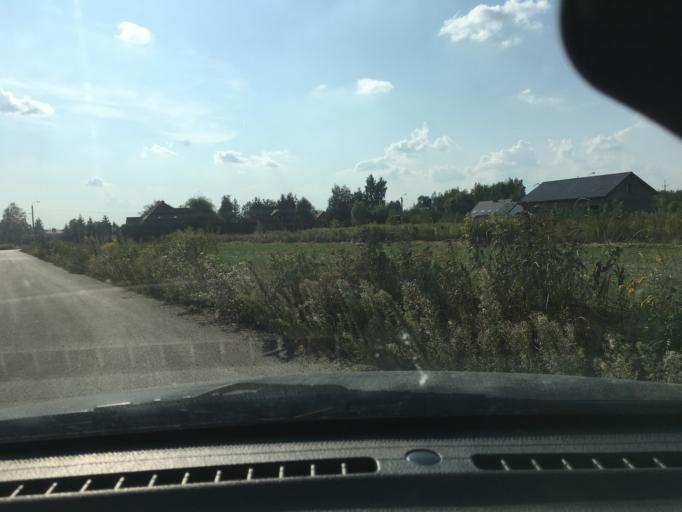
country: PL
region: Masovian Voivodeship
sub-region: Powiat piaseczynski
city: Lesznowola
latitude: 52.0516
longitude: 20.9343
